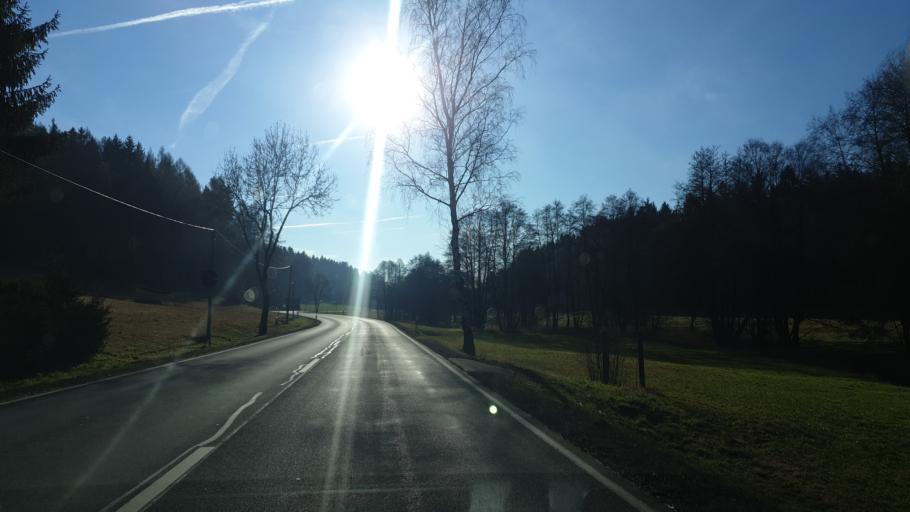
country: DE
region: Saxony
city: Bad Brambach
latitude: 50.2668
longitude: 12.3004
